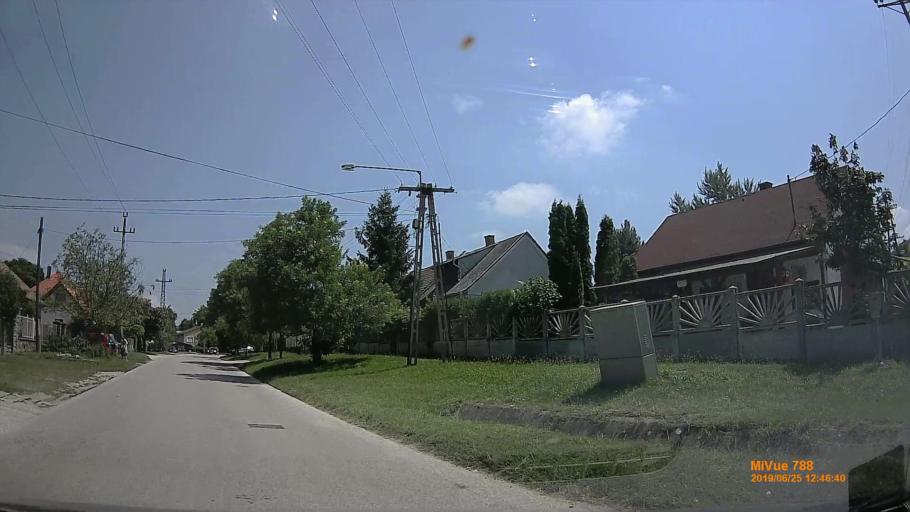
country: HU
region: Komarom-Esztergom
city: Esztergom
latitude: 47.8043
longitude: 18.7475
